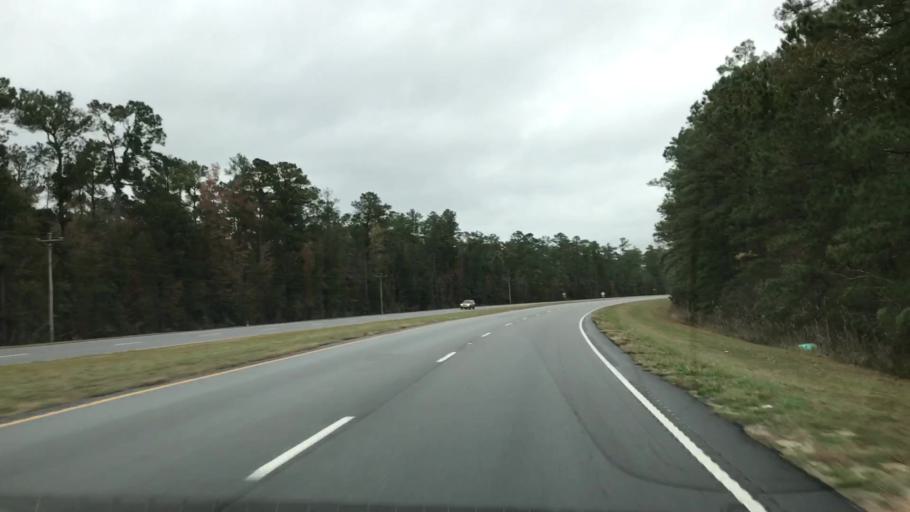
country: US
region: South Carolina
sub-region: Georgetown County
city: Georgetown
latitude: 33.2505
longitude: -79.3748
